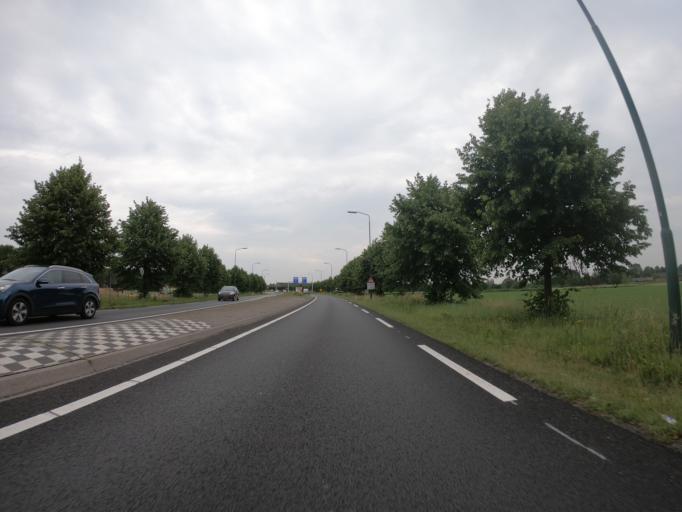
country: NL
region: North Brabant
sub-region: Gemeente Uden
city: Uden
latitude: 51.6487
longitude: 5.6067
